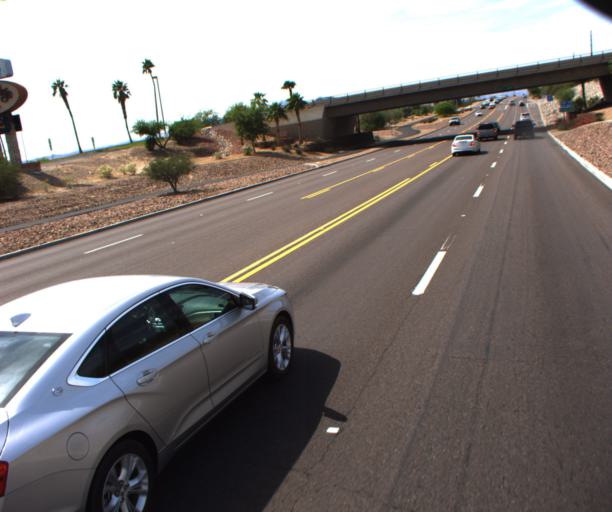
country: US
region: Arizona
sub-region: Mohave County
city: Lake Havasu City
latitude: 34.4728
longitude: -114.3445
